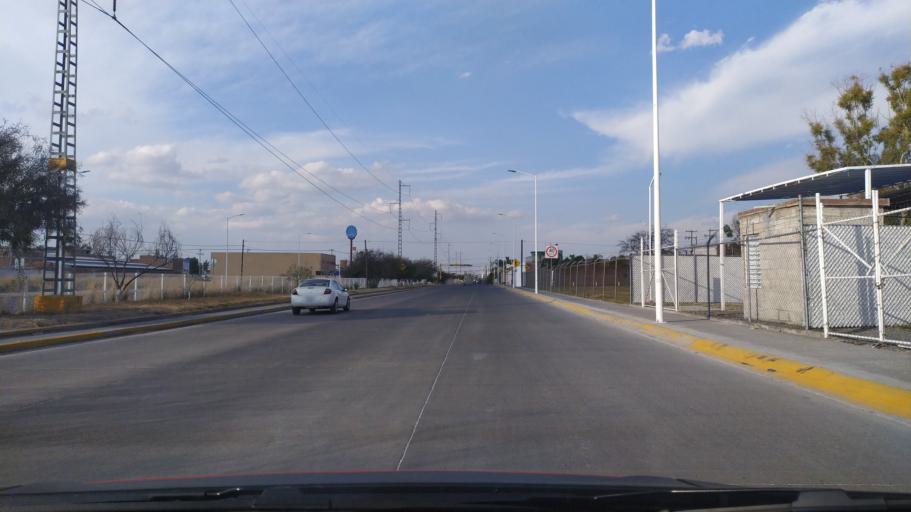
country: MX
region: Guanajuato
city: San Francisco del Rincon
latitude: 21.0152
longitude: -101.8697
